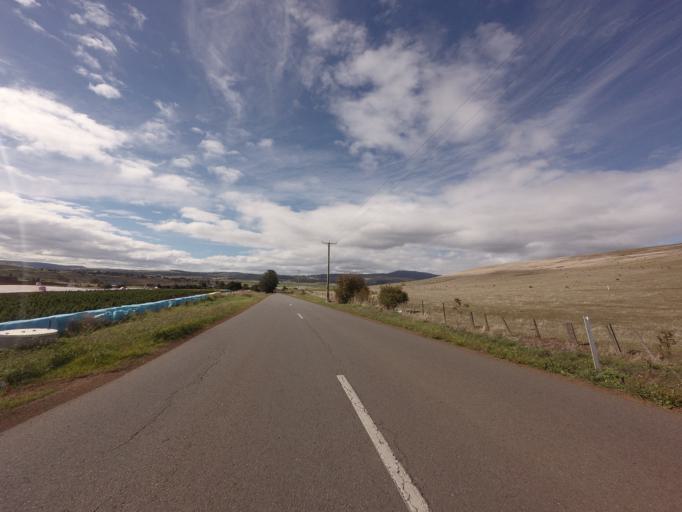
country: AU
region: Tasmania
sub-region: Derwent Valley
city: New Norfolk
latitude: -42.6969
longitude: 146.9312
